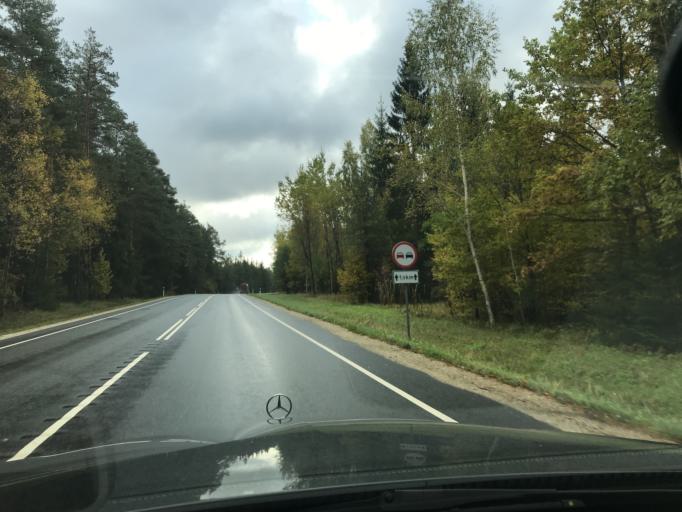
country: EE
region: Viljandimaa
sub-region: Karksi vald
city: Karksi-Nuia
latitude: 58.0298
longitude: 25.6520
